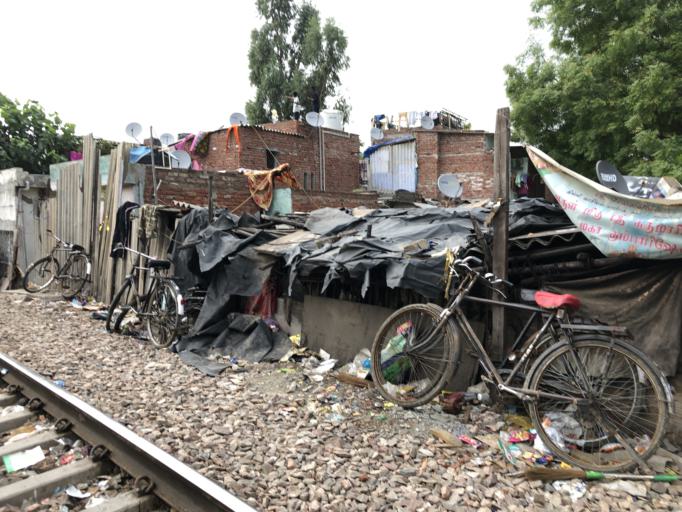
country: IN
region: NCT
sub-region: New Delhi
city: New Delhi
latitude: 28.5776
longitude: 77.2498
